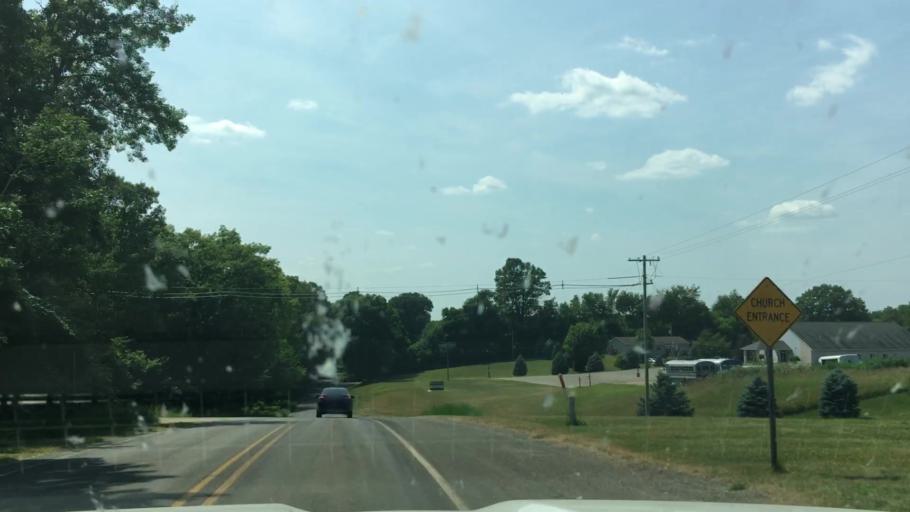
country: US
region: Michigan
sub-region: Kalamazoo County
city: Comstock Northwest
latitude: 42.4288
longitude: -85.5253
